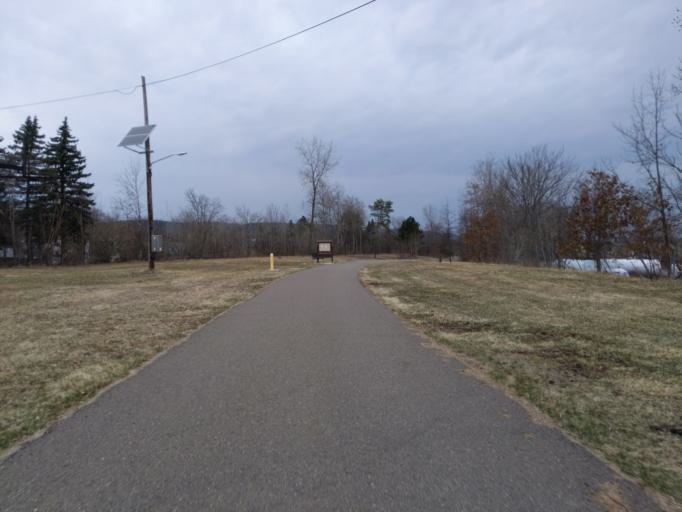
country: US
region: New York
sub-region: Chemung County
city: Elmira
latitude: 42.1011
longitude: -76.8076
